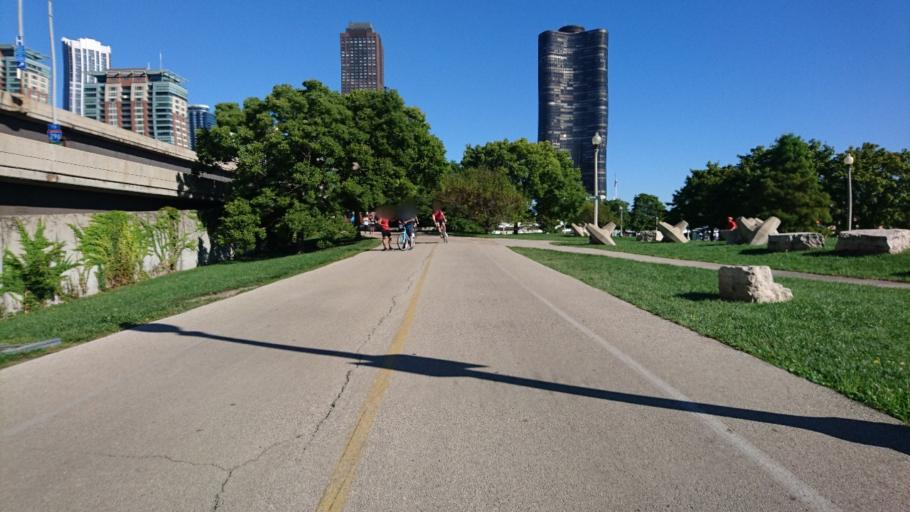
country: US
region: Illinois
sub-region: Cook County
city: Chicago
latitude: 41.8863
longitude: -87.6133
